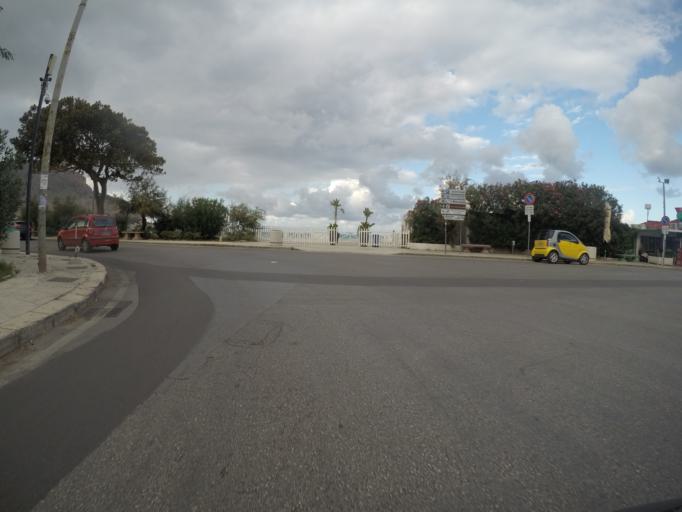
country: IT
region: Sicily
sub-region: Palermo
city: Palermo
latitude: 38.1969
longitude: 13.3320
